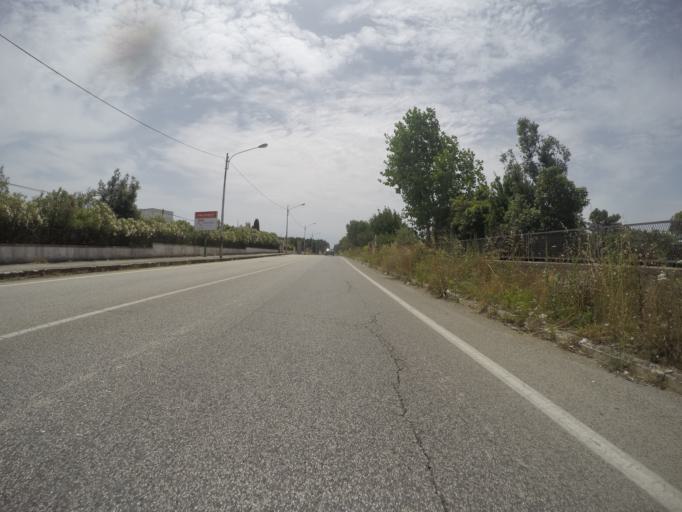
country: IT
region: Apulia
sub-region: Provincia di Taranto
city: Martina Franca
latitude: 40.6786
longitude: 17.3296
